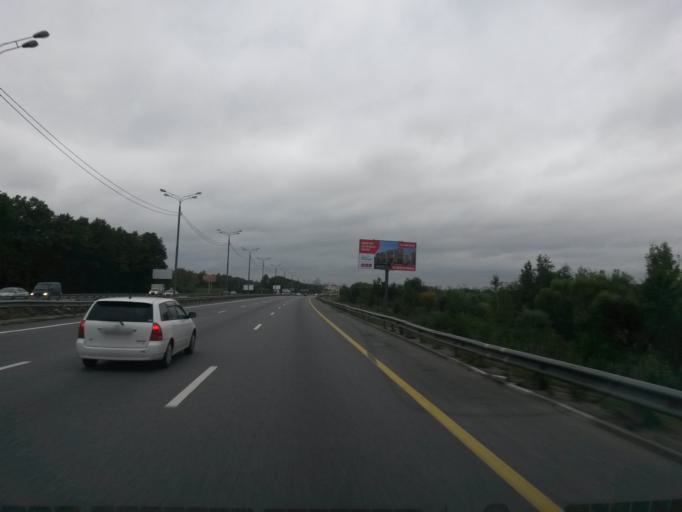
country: RU
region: Moskovskaya
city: Vidnoye
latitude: 55.5228
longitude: 37.7048
